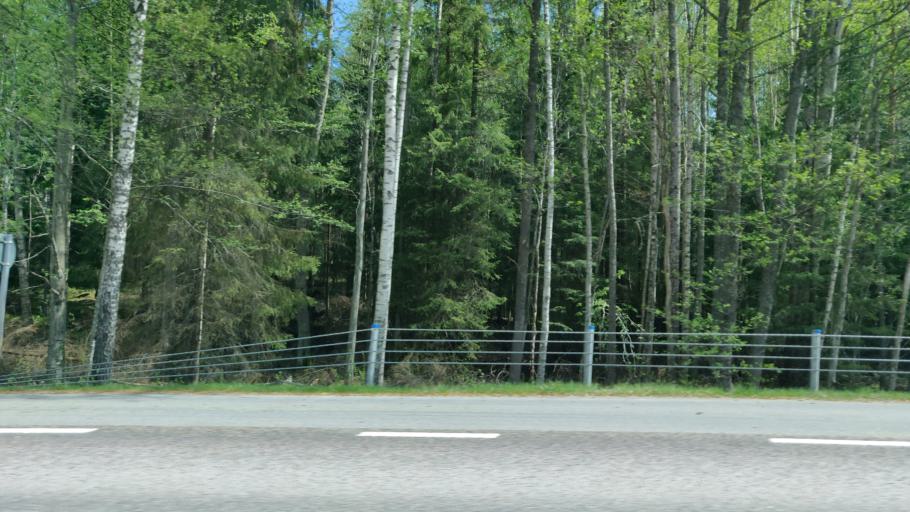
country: SE
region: Vaermland
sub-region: Karlstads Kommun
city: Molkom
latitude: 59.5276
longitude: 13.6179
